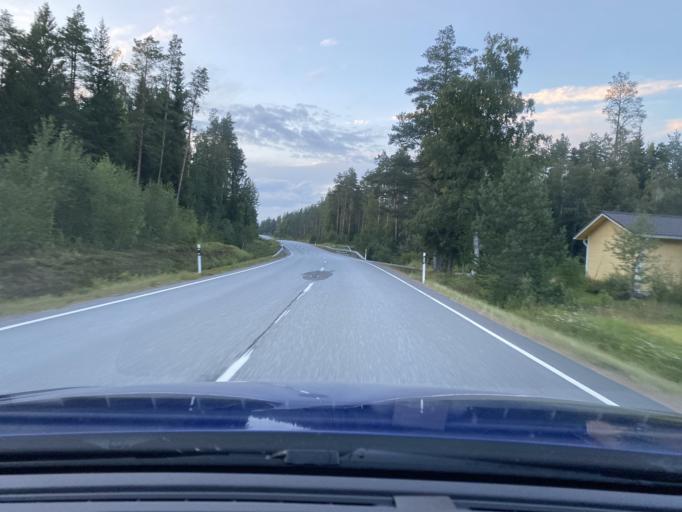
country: FI
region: Satakunta
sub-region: Pohjois-Satakunta
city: Honkajoki
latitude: 62.0373
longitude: 22.2408
